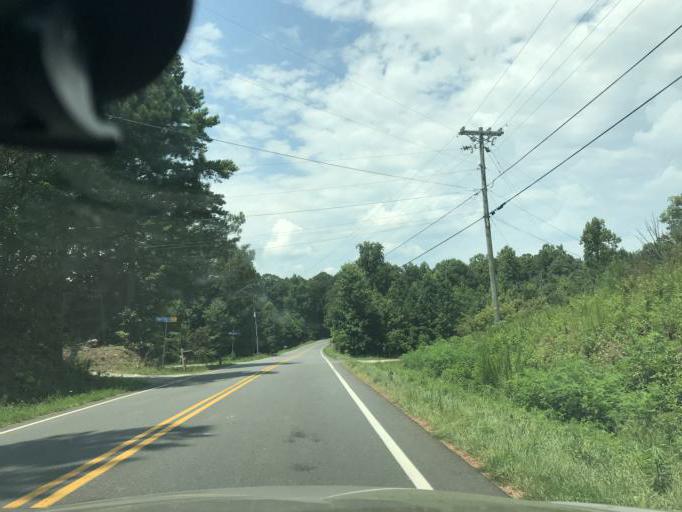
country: US
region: Georgia
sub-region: Dawson County
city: Dawsonville
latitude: 34.3371
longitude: -84.1540
